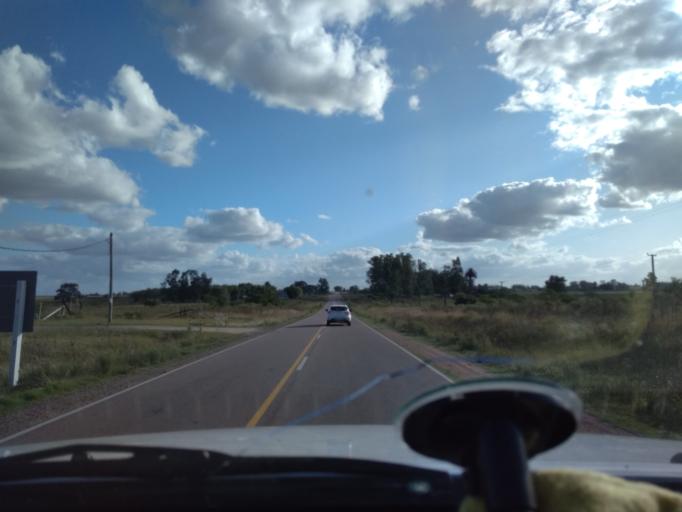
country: UY
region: Canelones
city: Tala
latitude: -34.3690
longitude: -55.7830
